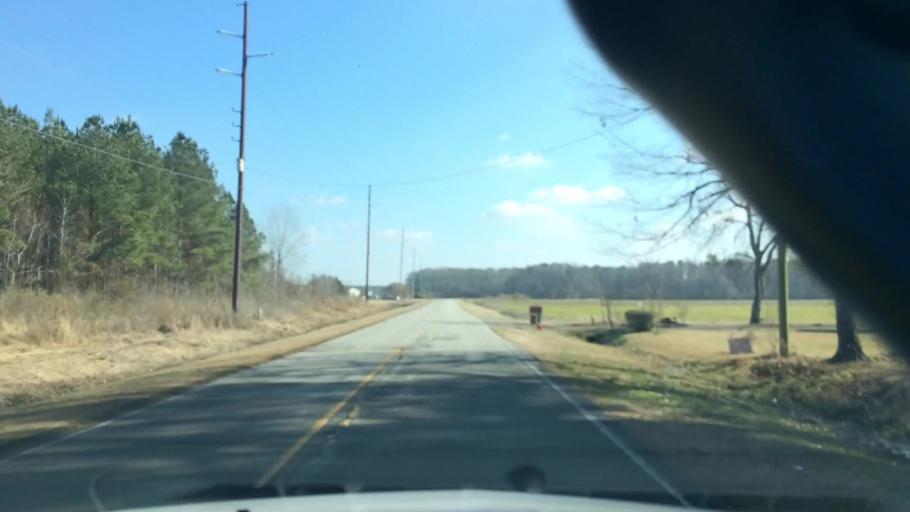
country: US
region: North Carolina
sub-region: Pitt County
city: Grifton
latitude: 35.4193
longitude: -77.4314
